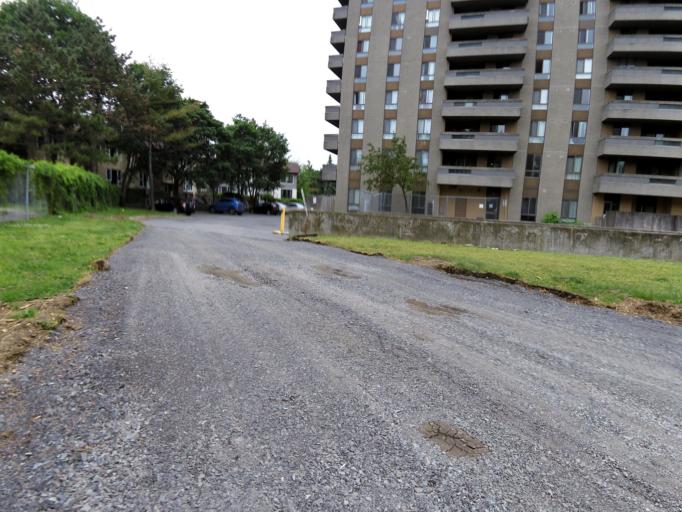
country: CA
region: Ontario
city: Bells Corners
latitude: 45.3332
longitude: -75.7859
